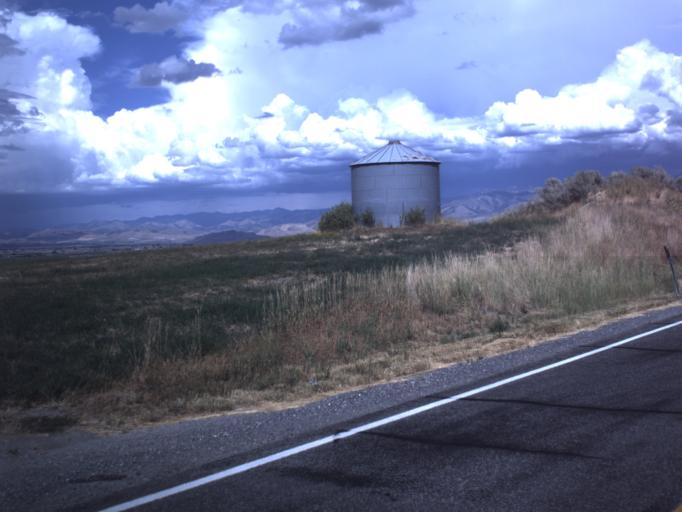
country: US
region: Utah
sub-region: Cache County
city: Lewiston
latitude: 41.9175
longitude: -111.9775
